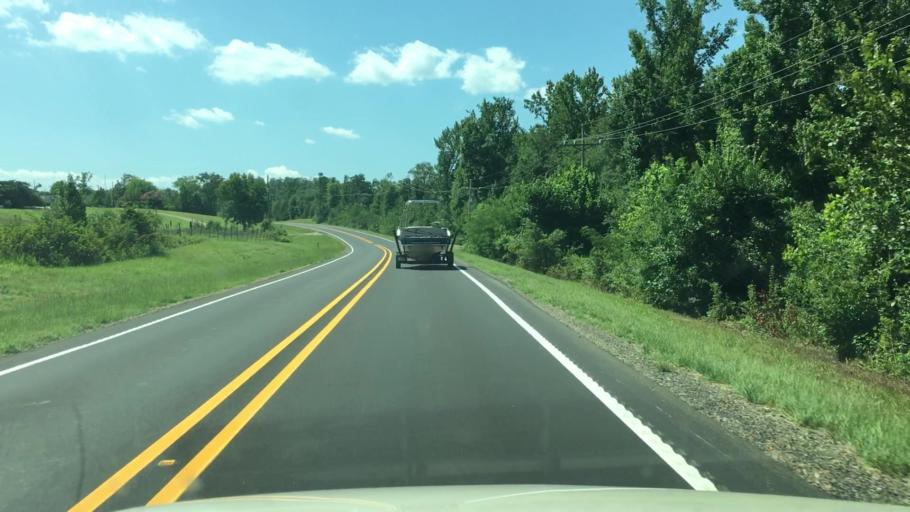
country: US
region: Arkansas
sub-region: Garland County
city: Rockwell
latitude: 34.5143
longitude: -93.2846
